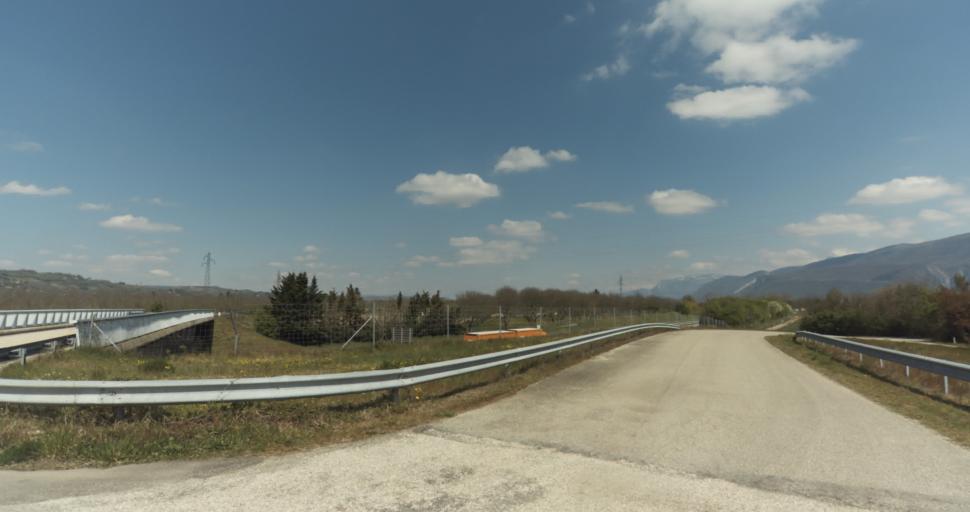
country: FR
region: Rhone-Alpes
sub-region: Departement de l'Isere
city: Saint-Romans
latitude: 45.1320
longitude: 5.3138
